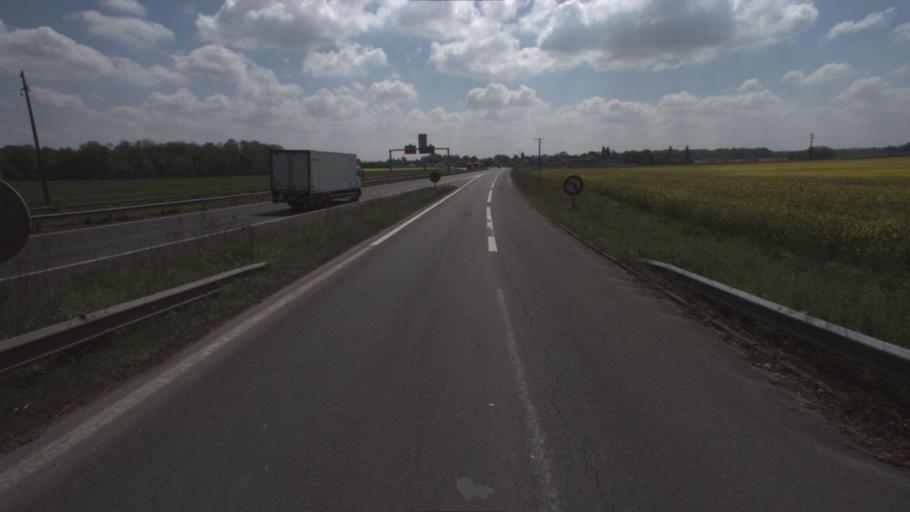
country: FR
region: Ile-de-France
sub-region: Departement de Seine-et-Marne
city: Fontenay-Tresigny
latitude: 48.7170
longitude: 2.8484
